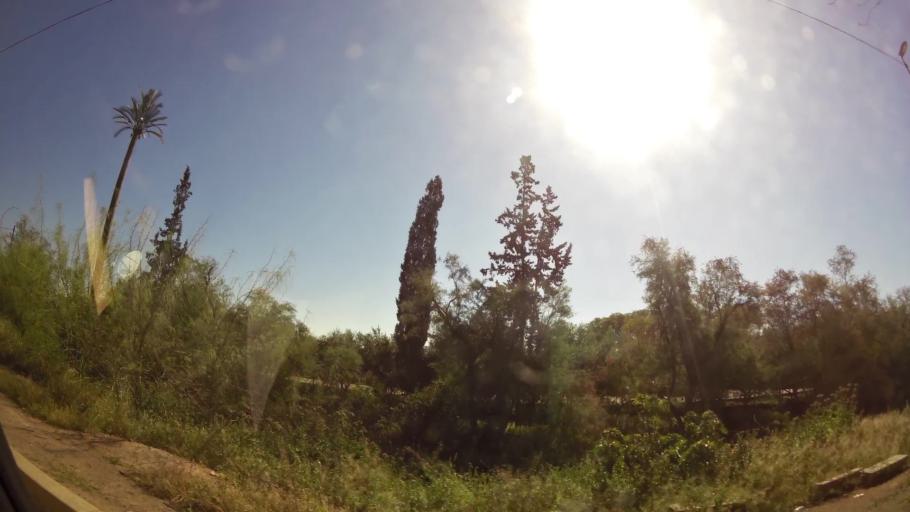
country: MA
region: Marrakech-Tensift-Al Haouz
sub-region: Marrakech
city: Marrakesh
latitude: 31.6620
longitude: -7.9348
